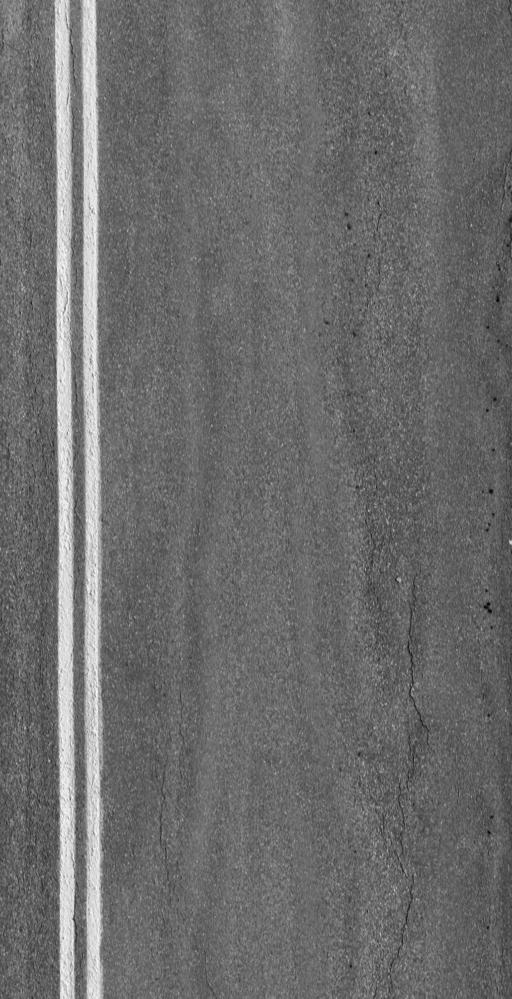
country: US
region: Vermont
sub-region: Addison County
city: Vergennes
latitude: 44.3089
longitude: -73.2682
